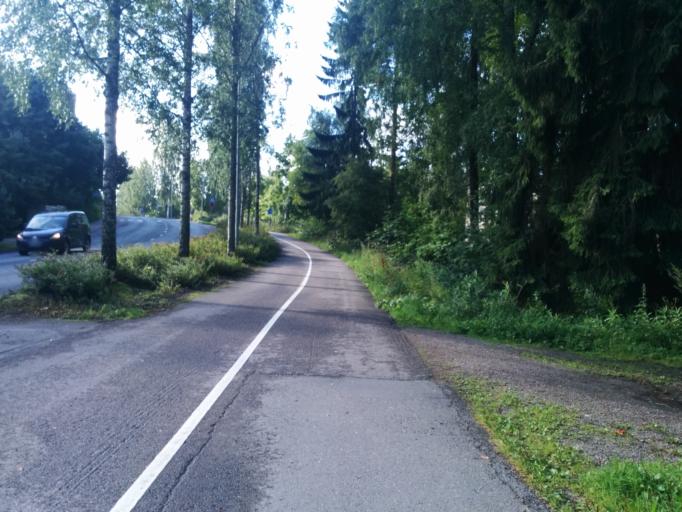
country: FI
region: Uusimaa
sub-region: Helsinki
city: Kerava
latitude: 60.4086
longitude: 25.0969
